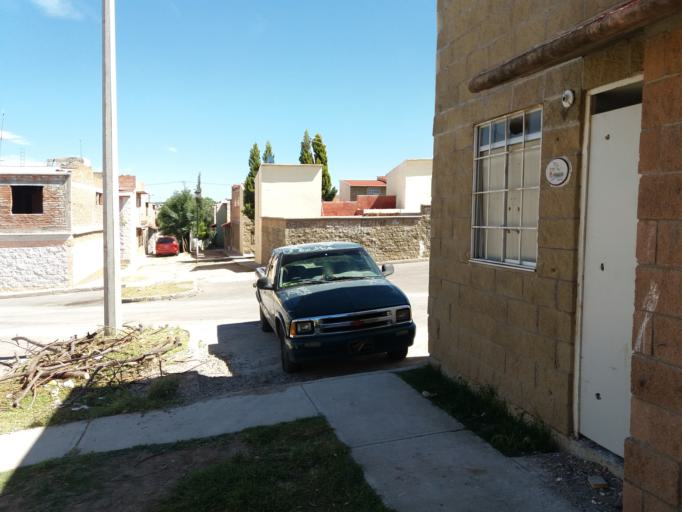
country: MX
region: Aguascalientes
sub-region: Aguascalientes
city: Aguascalientes
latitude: 21.8735
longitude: -102.2361
